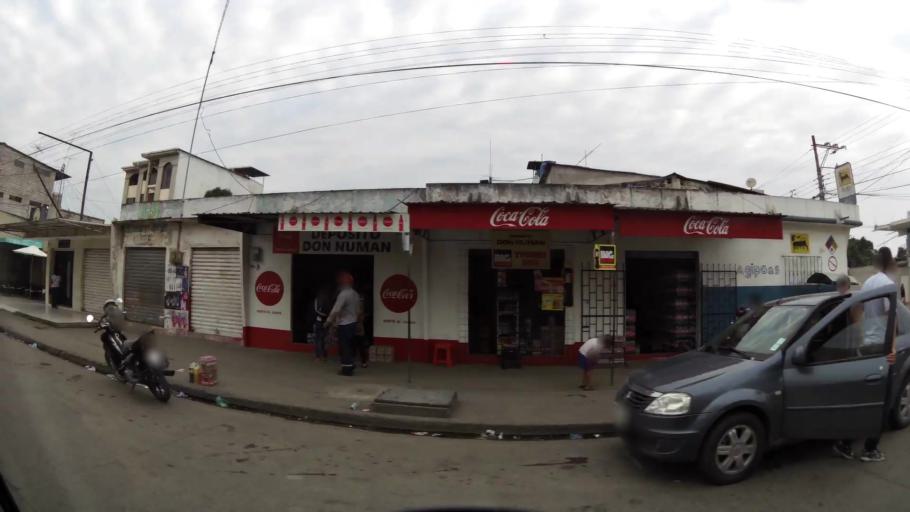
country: EC
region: El Oro
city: Machala
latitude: -3.2552
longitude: -79.9539
